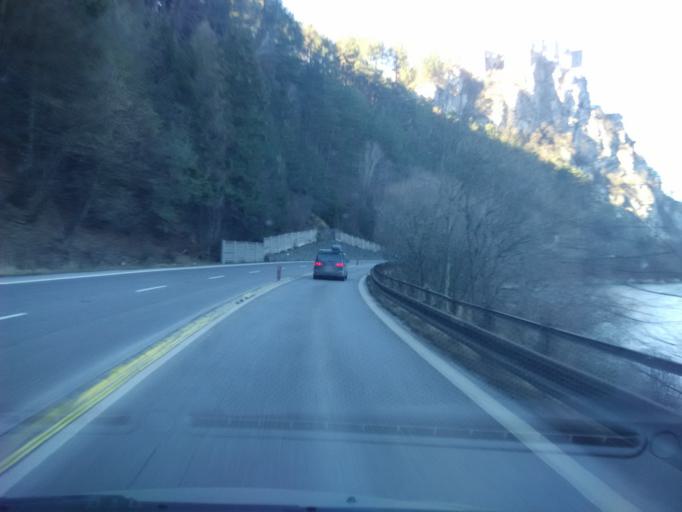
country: SK
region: Zilinsky
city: Krasnany
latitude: 49.1720
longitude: 18.8640
